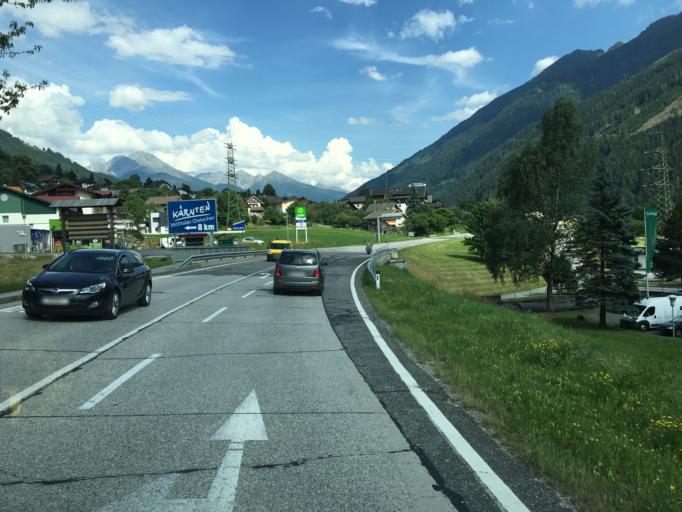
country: AT
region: Carinthia
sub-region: Politischer Bezirk Spittal an der Drau
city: Flattach
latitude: 46.9355
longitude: 13.1091
